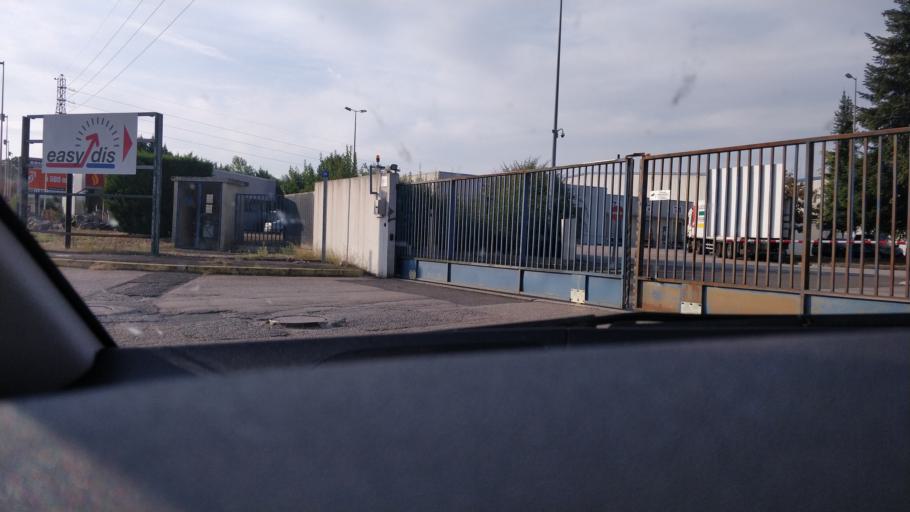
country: FR
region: Limousin
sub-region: Departement de la Haute-Vienne
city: Chaptelat
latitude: 45.8847
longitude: 1.2818
